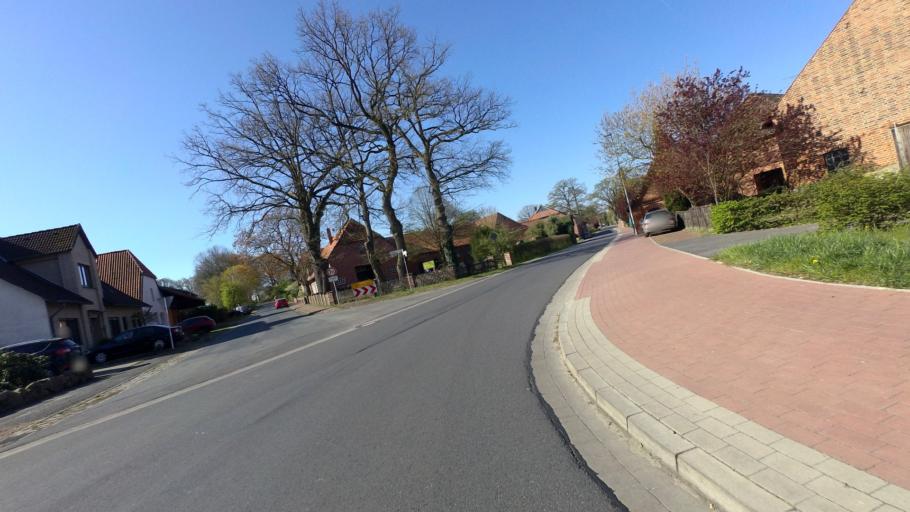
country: DE
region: Lower Saxony
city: Steimbke
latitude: 52.6541
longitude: 9.3887
